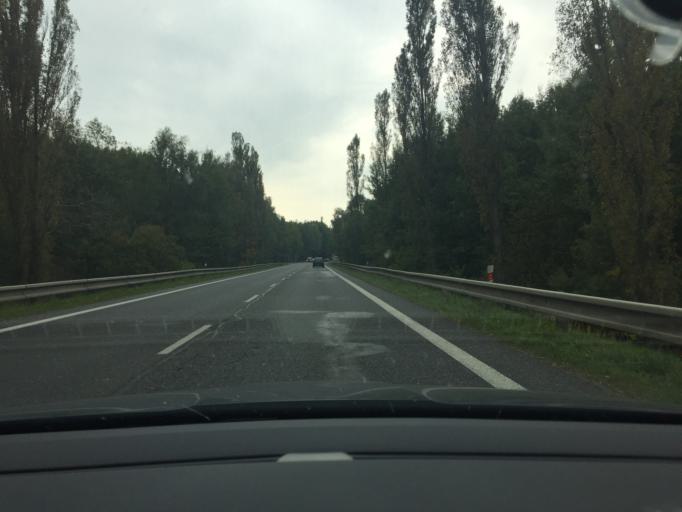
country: CZ
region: Central Bohemia
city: Milin
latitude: 49.6607
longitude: 14.0596
